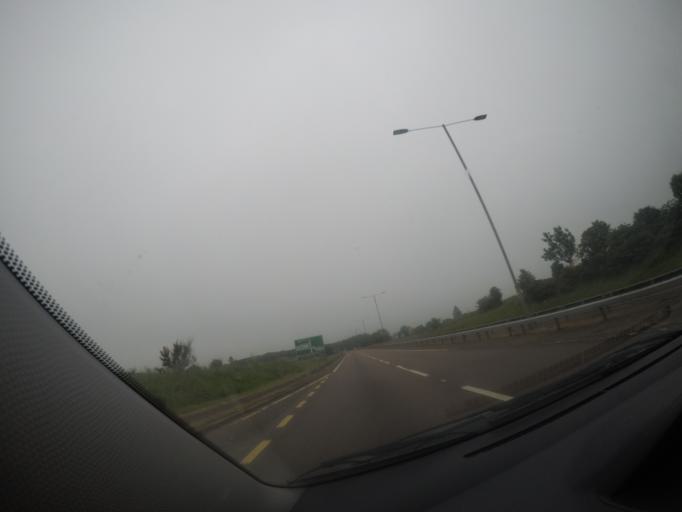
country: GB
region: Scotland
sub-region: Dundee City
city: Dundee
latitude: 56.5258
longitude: -2.9447
